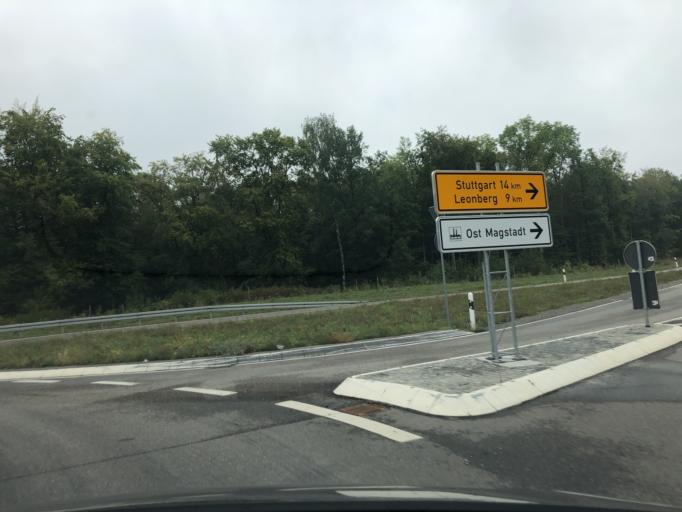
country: DE
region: Baden-Wuerttemberg
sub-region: Regierungsbezirk Stuttgart
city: Sindelfingen
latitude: 48.7379
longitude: 9.0232
